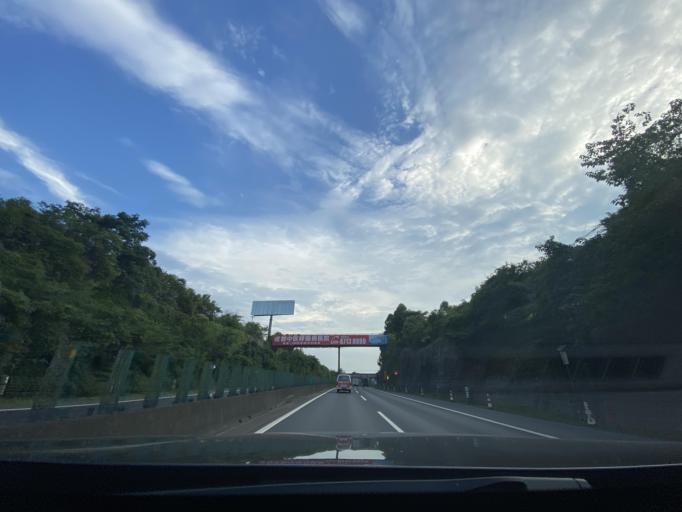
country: CN
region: Sichuan
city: Luojiang
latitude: 31.4063
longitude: 104.5743
